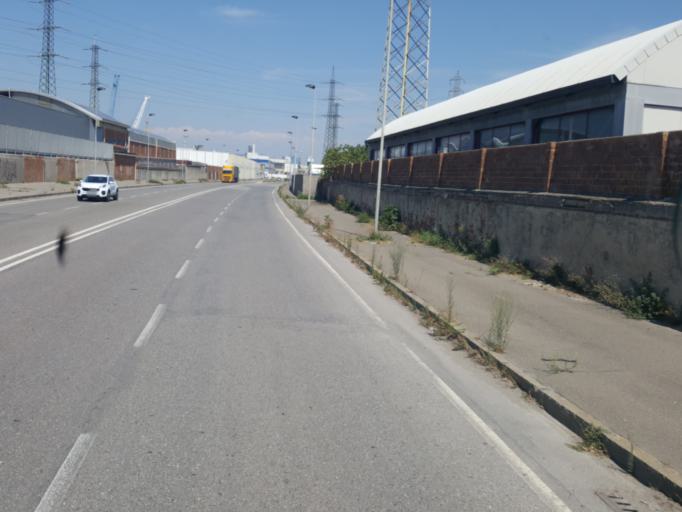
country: IT
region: Tuscany
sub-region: Provincia di Livorno
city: Livorno
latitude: 43.5682
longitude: 10.3139
